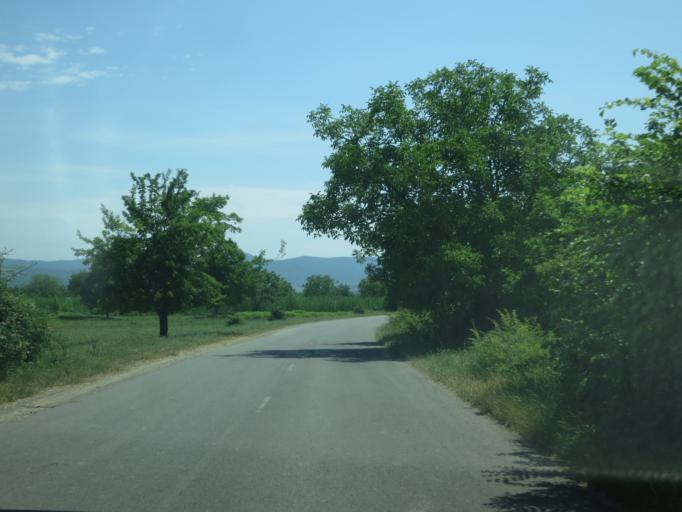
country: GE
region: Kakheti
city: Sagarejo
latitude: 41.6938
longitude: 45.3938
